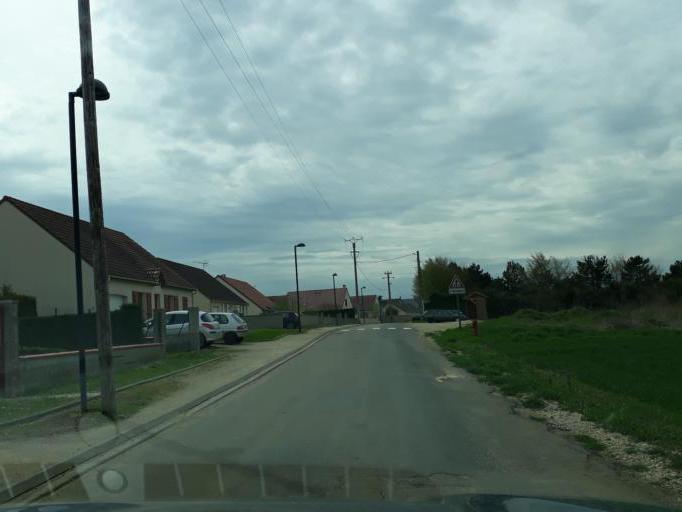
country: FR
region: Centre
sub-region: Departement du Loiret
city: Epieds-en-Beauce
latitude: 47.9492
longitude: 1.6250
